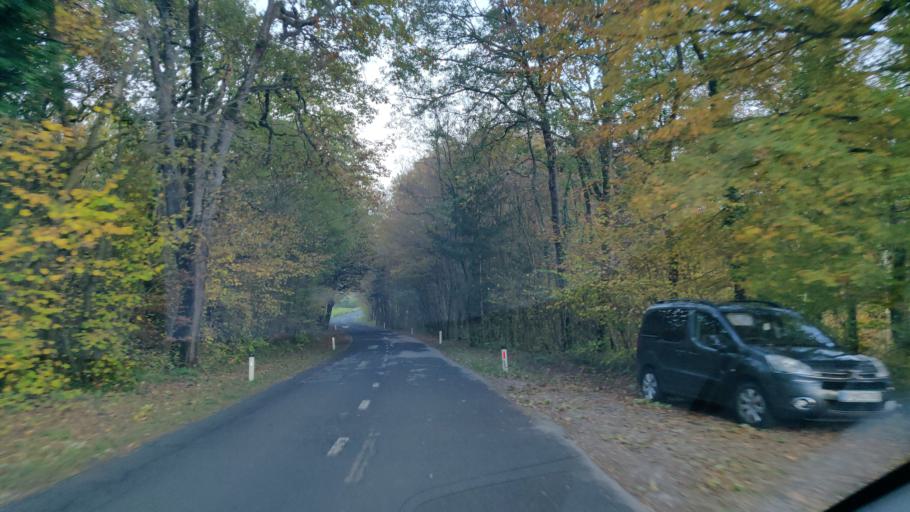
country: SI
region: Sezana
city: Sezana
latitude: 45.7661
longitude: 13.8892
